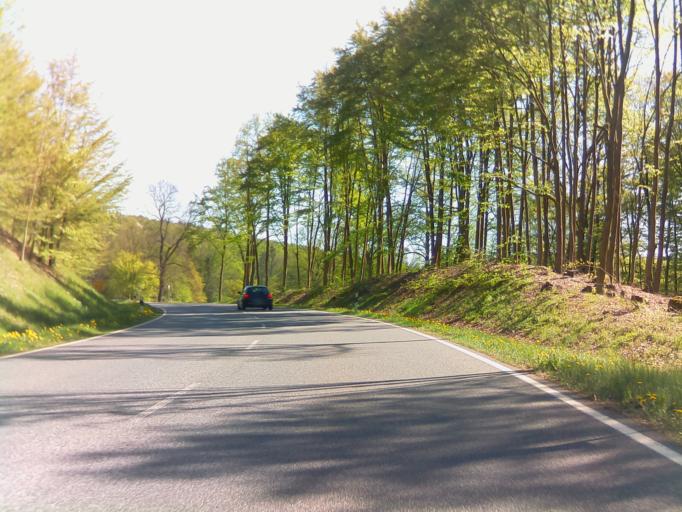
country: DE
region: Hesse
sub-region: Regierungsbezirk Giessen
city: Lauterbach
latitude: 50.6060
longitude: 9.3916
